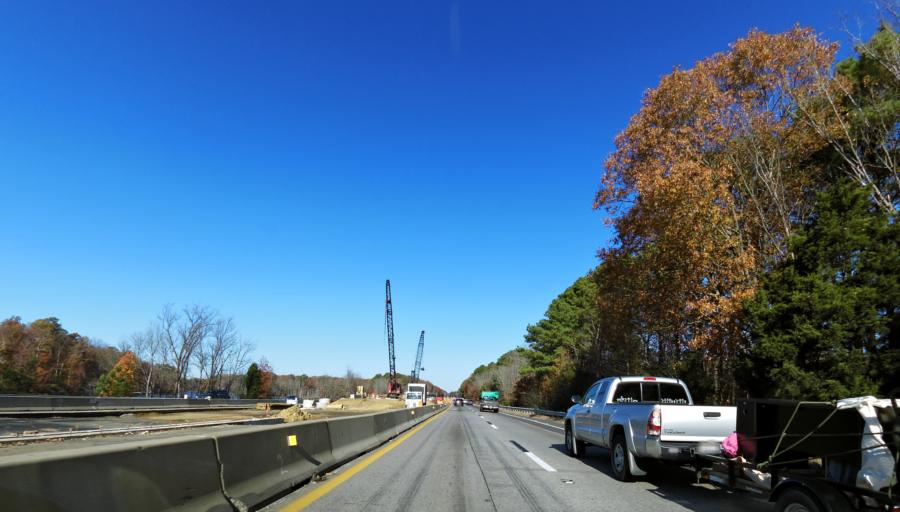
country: US
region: Virginia
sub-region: York County
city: Yorktown
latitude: 37.1845
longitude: -76.5568
